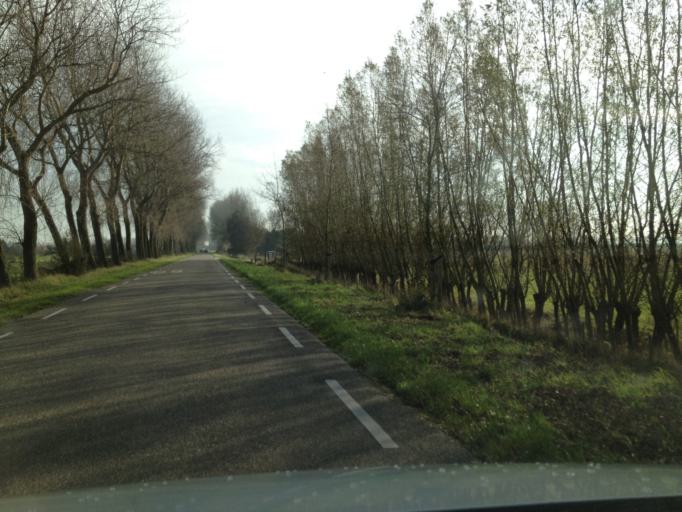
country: NL
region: Zeeland
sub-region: Gemeente Sluis
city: Sluis
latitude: 51.3514
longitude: 3.3760
